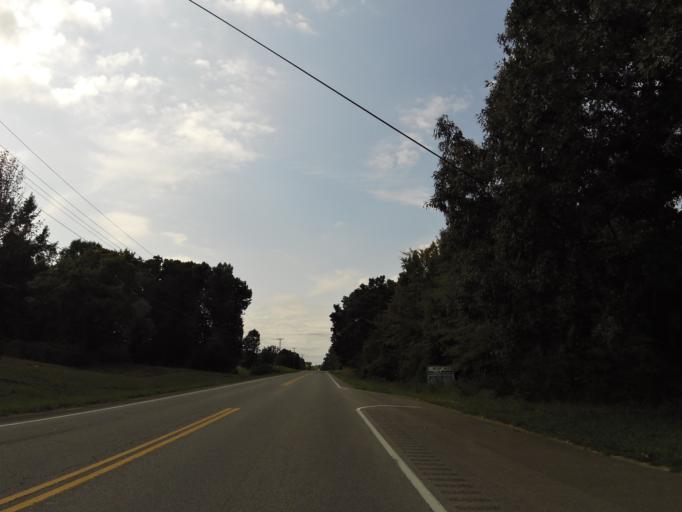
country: US
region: Tennessee
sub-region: Humphreys County
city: Waverly
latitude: 35.8738
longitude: -87.8053
